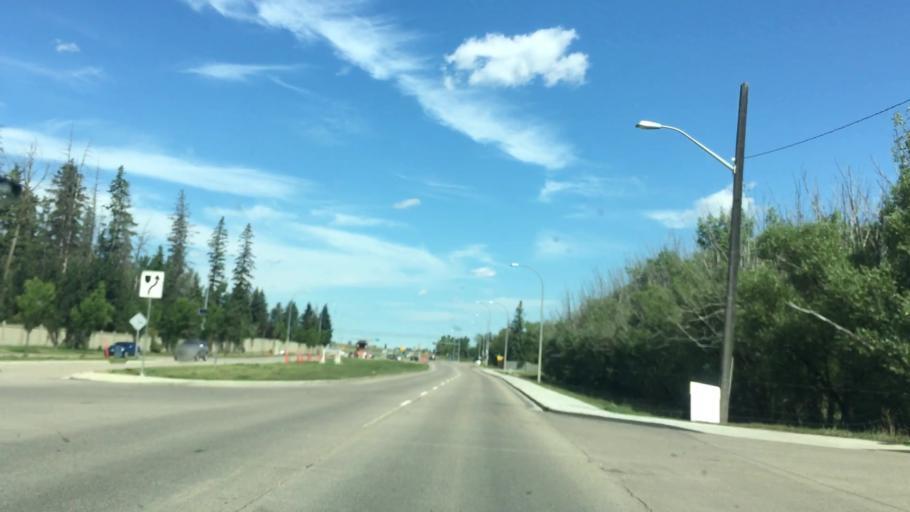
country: CA
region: Alberta
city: Beaumont
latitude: 53.4266
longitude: -113.5164
